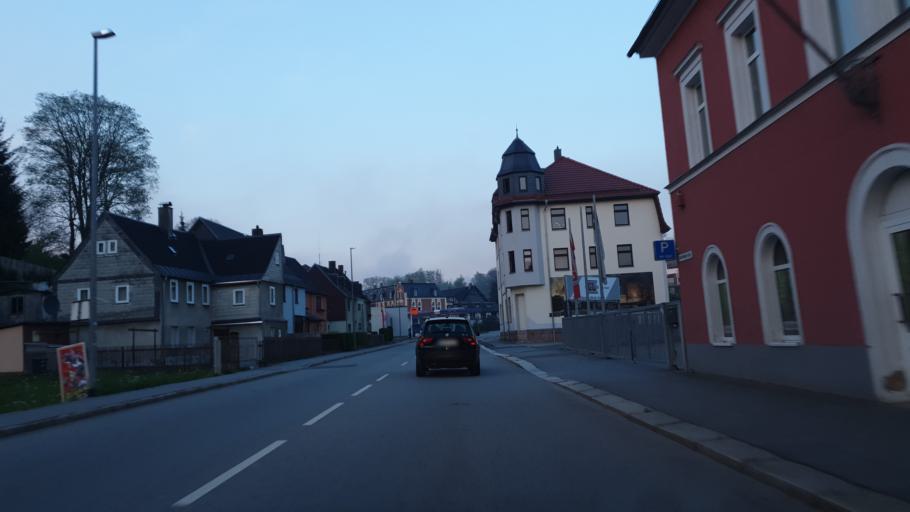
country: DE
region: Saxony
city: Lossnitz
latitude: 50.6149
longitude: 12.7249
